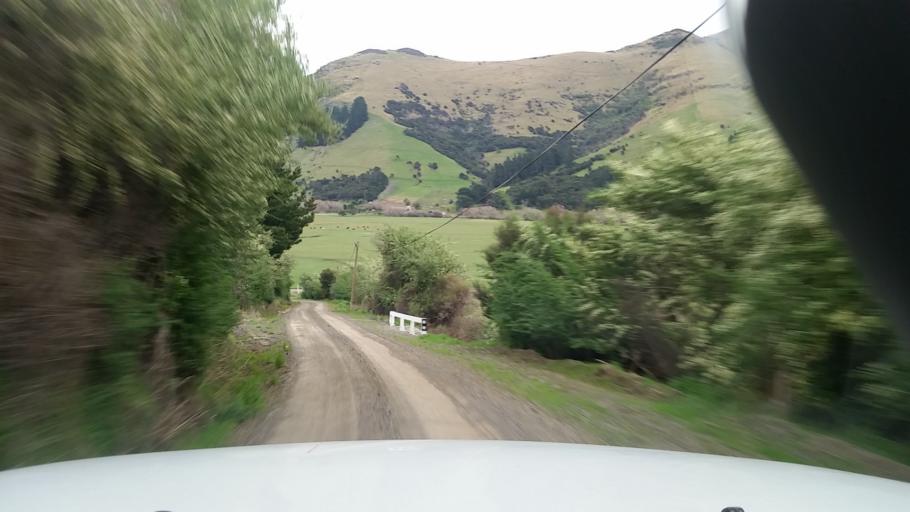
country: NZ
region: Canterbury
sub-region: Christchurch City
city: Christchurch
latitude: -43.7781
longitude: 172.7936
